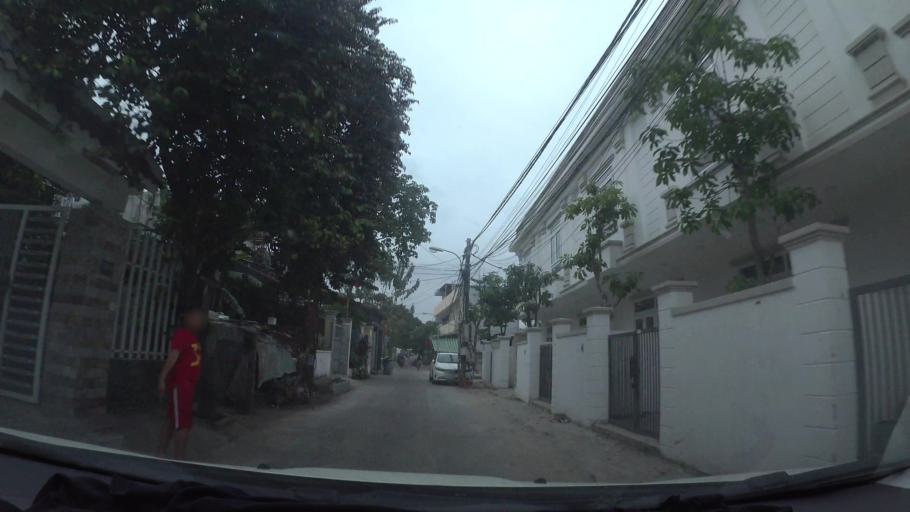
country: VN
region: Da Nang
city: Lien Chieu
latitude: 16.0853
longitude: 108.1529
